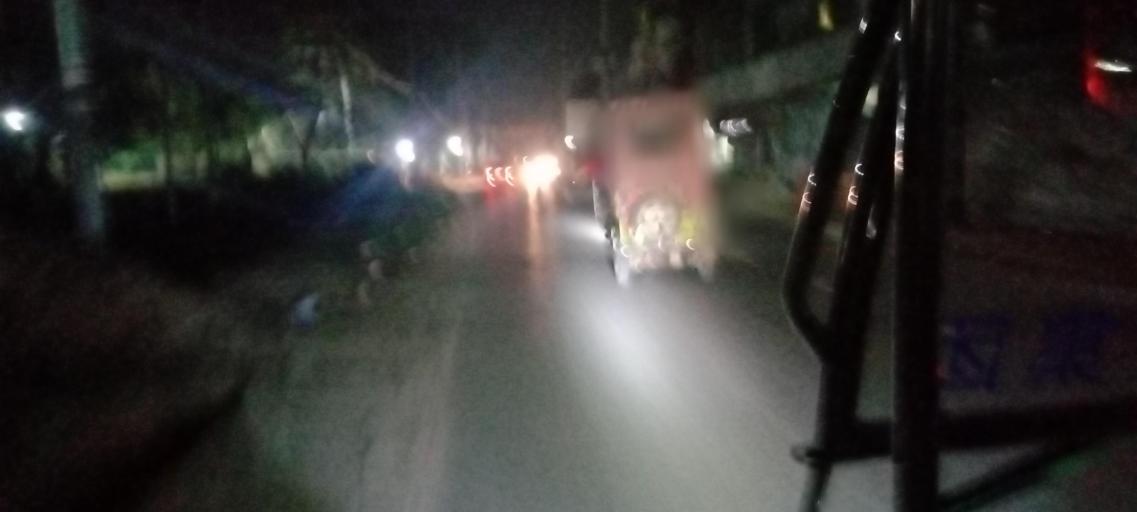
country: BD
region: Dhaka
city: Azimpur
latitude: 23.7001
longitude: 90.3706
